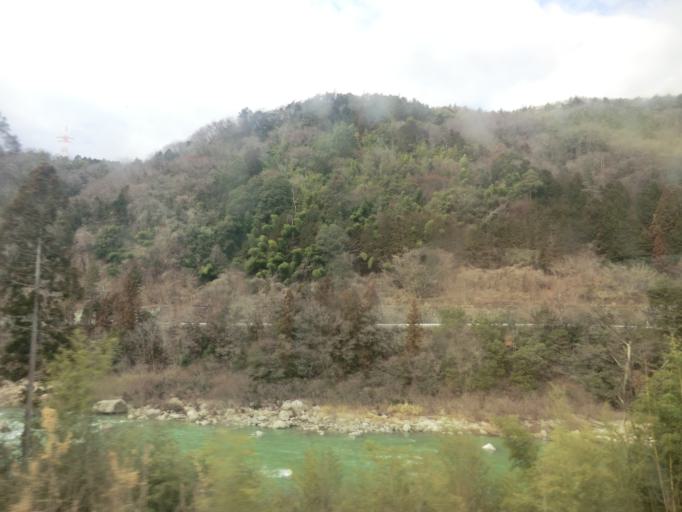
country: JP
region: Gifu
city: Nakatsugawa
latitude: 35.5826
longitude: 137.5342
